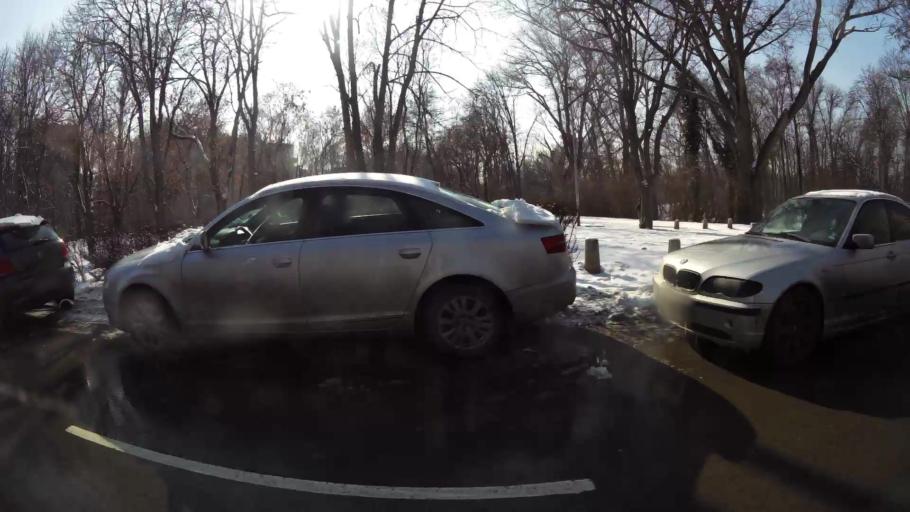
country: BG
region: Sofia-Capital
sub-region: Stolichna Obshtina
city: Sofia
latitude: 42.6744
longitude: 23.3104
